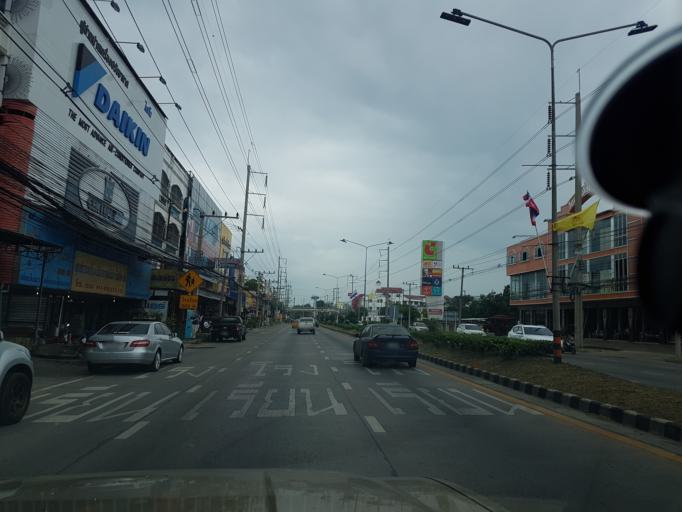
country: TH
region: Lop Buri
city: Lop Buri
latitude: 14.7971
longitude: 100.6639
